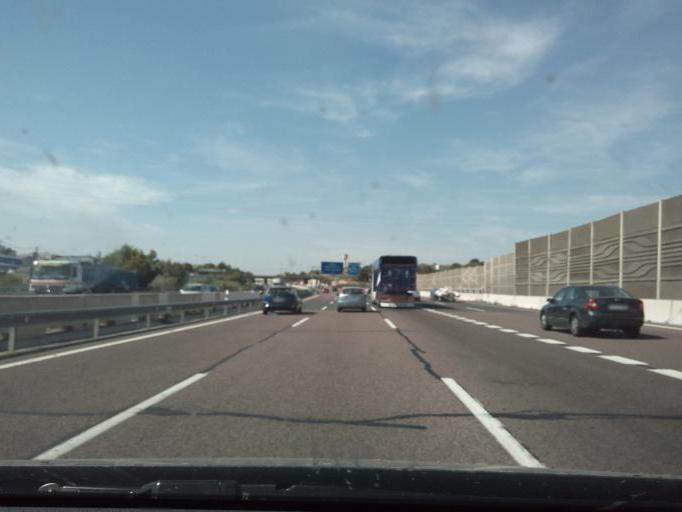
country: ES
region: Valencia
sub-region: Provincia de Valencia
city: Manises
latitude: 39.5245
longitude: -0.4714
